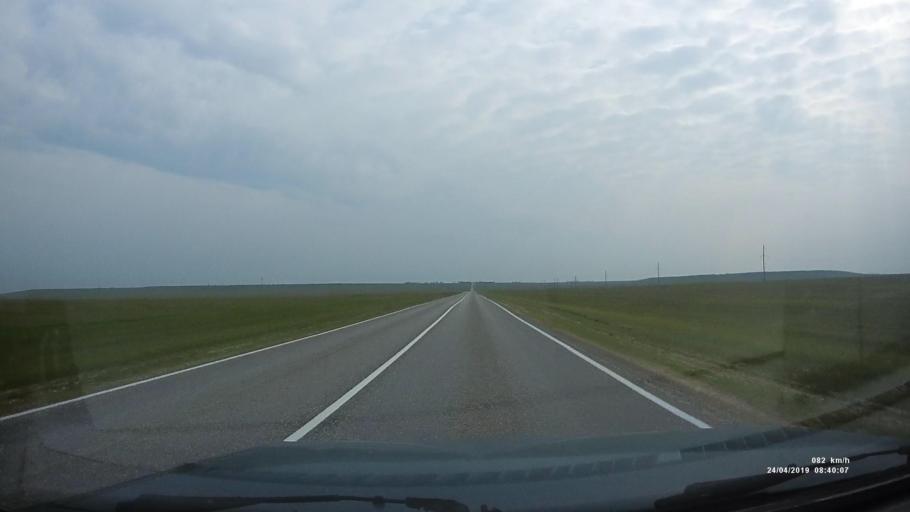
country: RU
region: Kalmykiya
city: Arshan'
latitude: 46.2246
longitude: 43.9952
